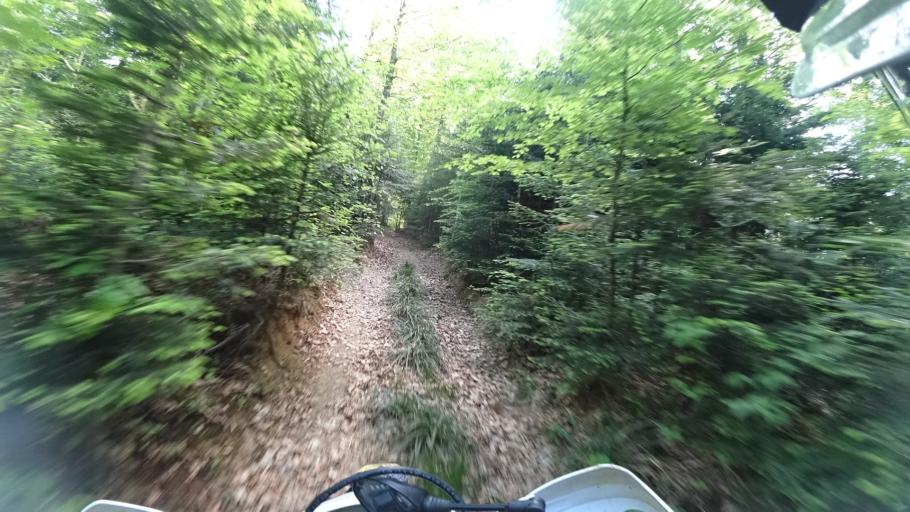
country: HR
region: Krapinsko-Zagorska
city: Oroslavje
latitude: 45.9412
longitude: 15.9425
